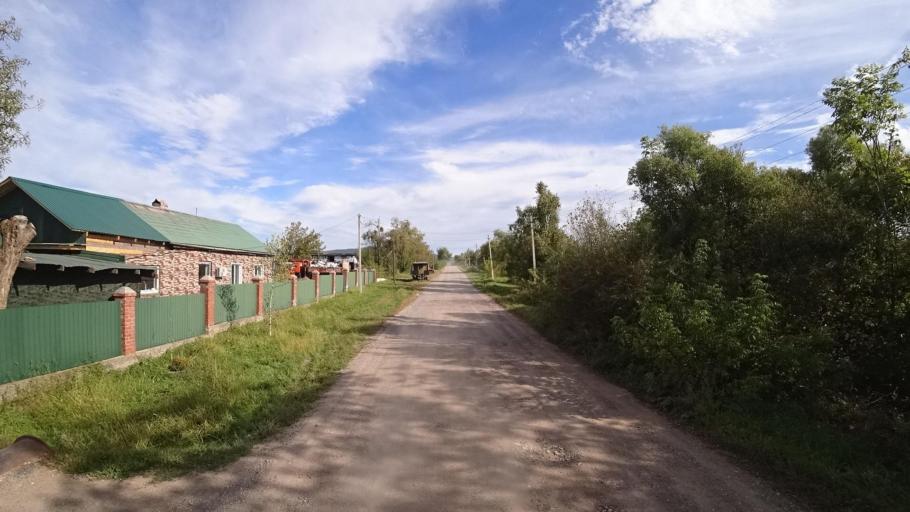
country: RU
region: Primorskiy
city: Dostoyevka
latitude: 44.3050
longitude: 133.4542
